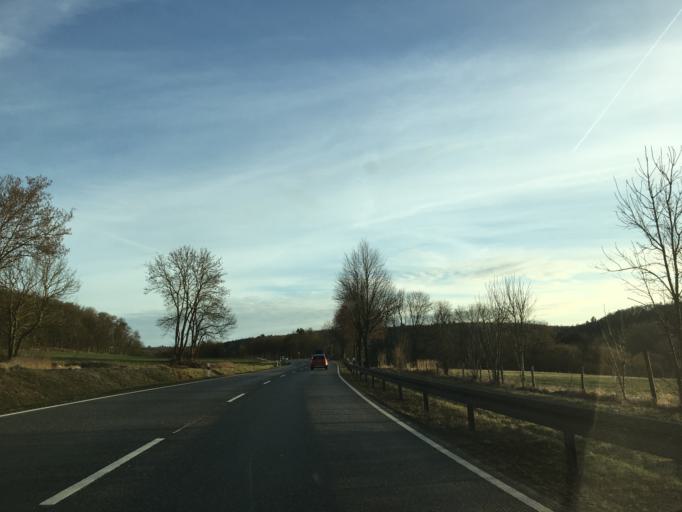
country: DE
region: Hesse
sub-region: Regierungsbezirk Giessen
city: Alsfeld
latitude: 50.7290
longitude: 9.2841
